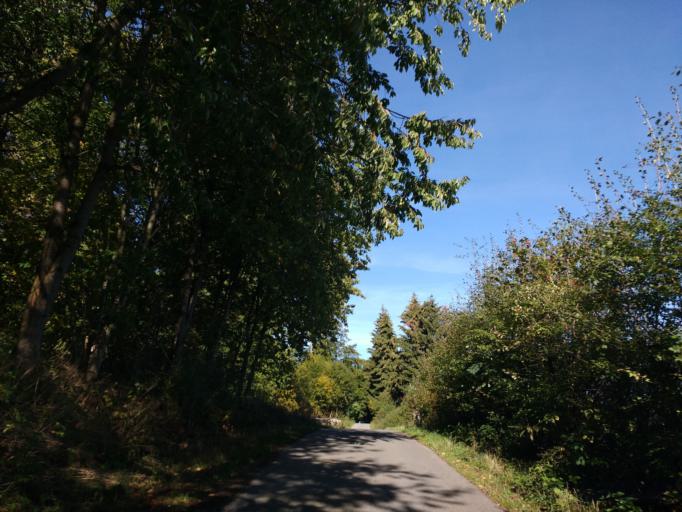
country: DE
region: North Rhine-Westphalia
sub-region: Regierungsbezirk Detmold
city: Willebadessen
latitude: 51.6296
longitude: 9.0076
